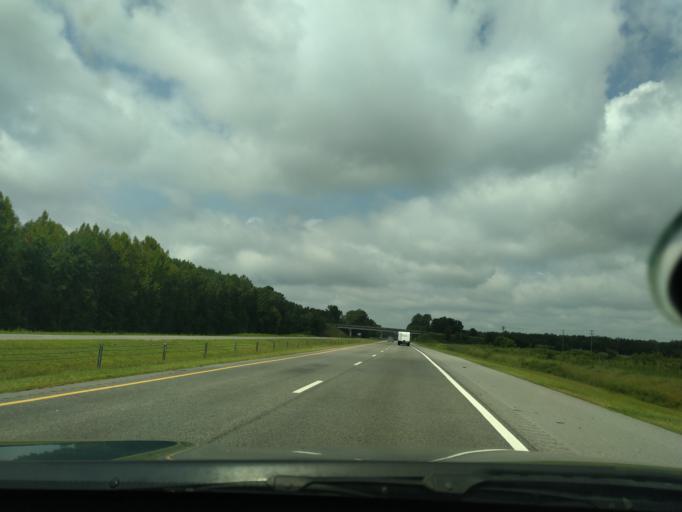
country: US
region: North Carolina
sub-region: Martin County
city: Robersonville
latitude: 35.8336
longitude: -77.3148
